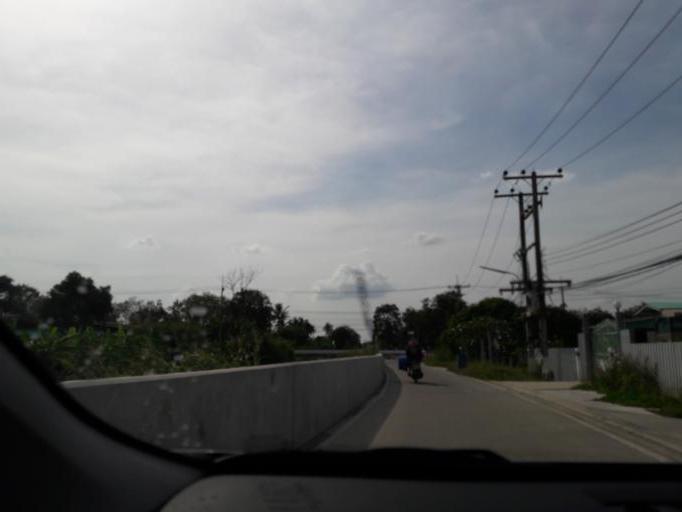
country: TH
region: Ang Thong
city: Ang Thong
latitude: 14.5882
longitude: 100.4420
